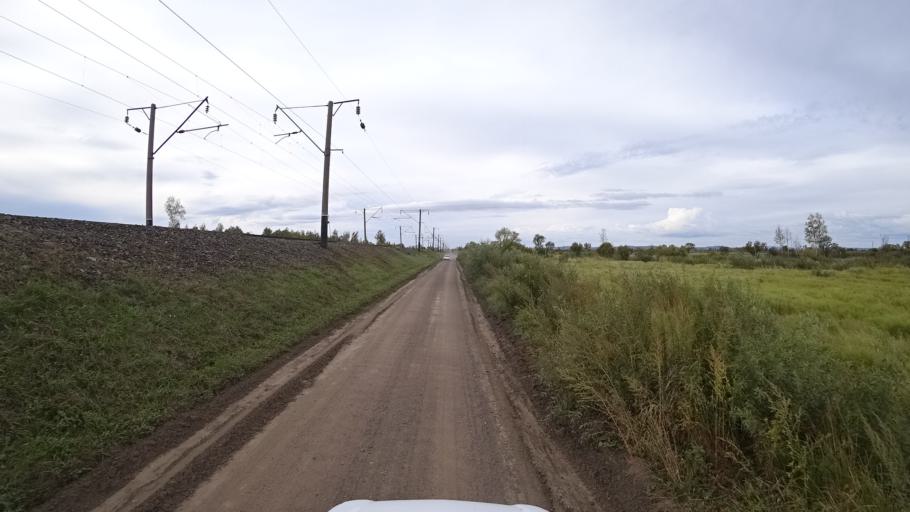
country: RU
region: Amur
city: Arkhara
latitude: 49.3549
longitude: 130.1551
